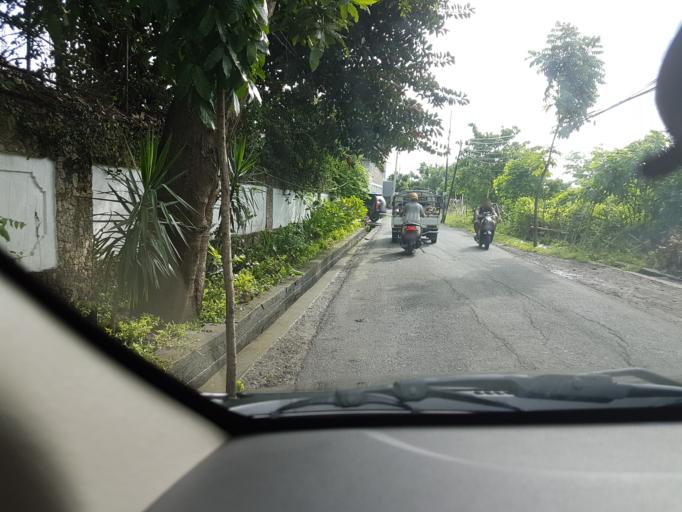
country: ID
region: Bali
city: Kuta
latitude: -8.6831
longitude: 115.1733
